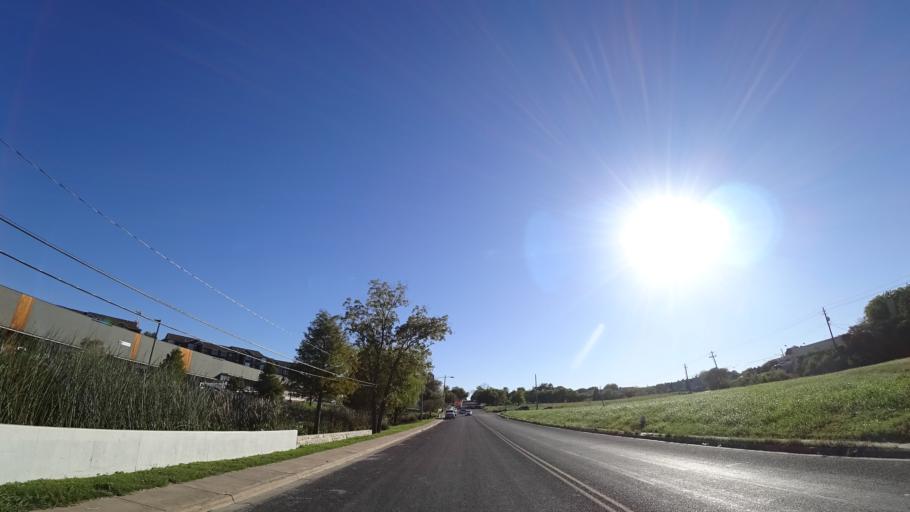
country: US
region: Texas
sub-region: Travis County
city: Austin
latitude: 30.2364
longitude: -97.7268
